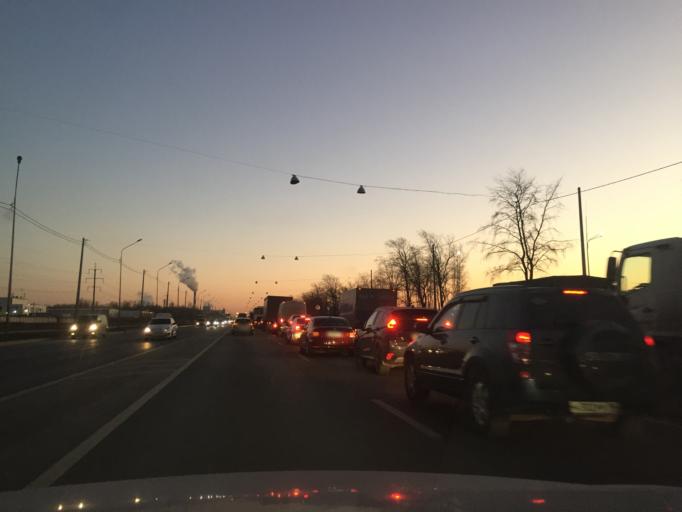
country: RU
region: St.-Petersburg
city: Obukhovo
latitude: 59.8562
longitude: 30.4230
